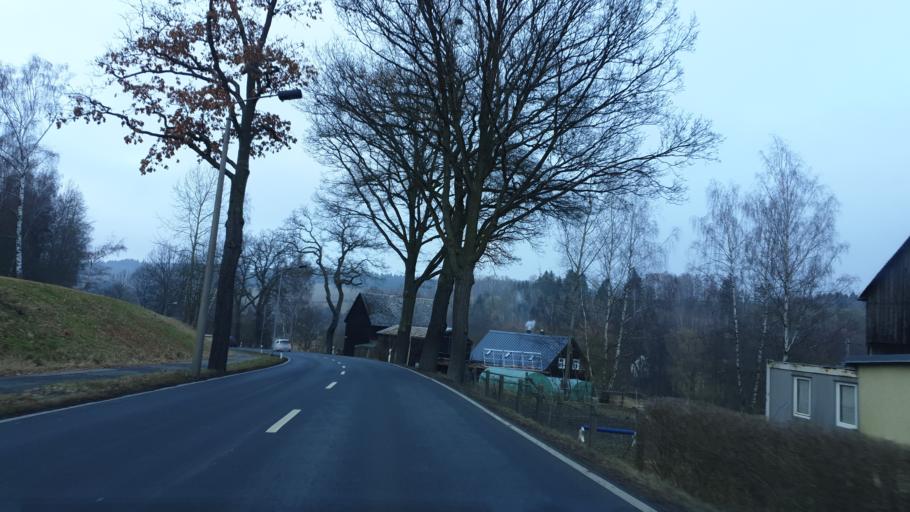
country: DE
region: Saxony
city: Adorf
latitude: 50.2893
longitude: 12.2726
